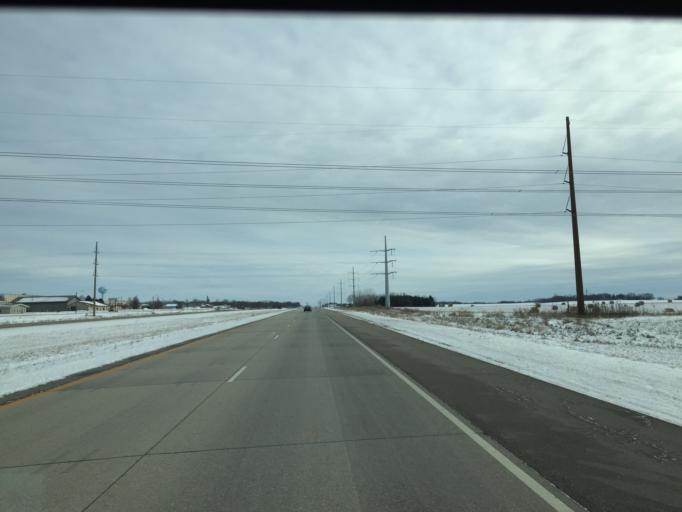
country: US
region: Minnesota
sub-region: Olmsted County
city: Byron
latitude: 44.0283
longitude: -92.6693
